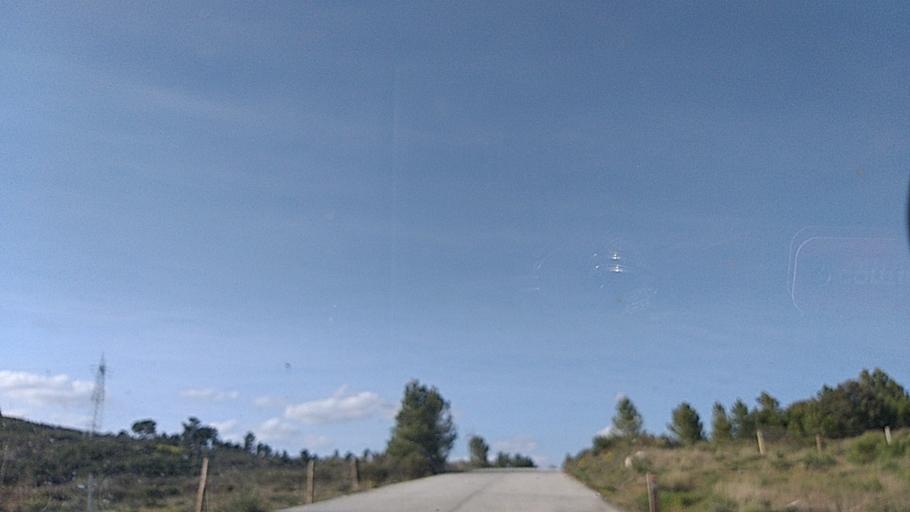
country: PT
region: Guarda
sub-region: Celorico da Beira
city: Celorico da Beira
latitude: 40.6509
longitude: -7.3967
